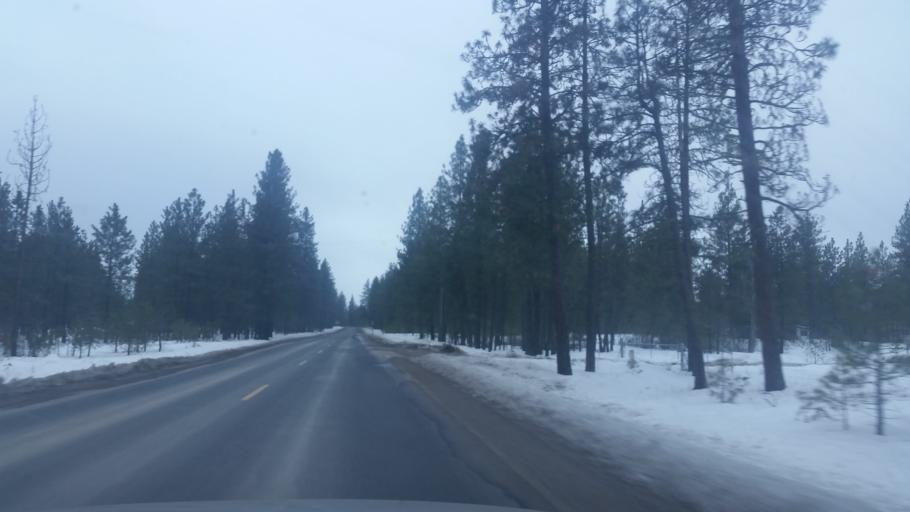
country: US
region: Washington
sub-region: Spokane County
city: Fairchild Air Force Base
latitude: 47.8576
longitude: -117.8463
